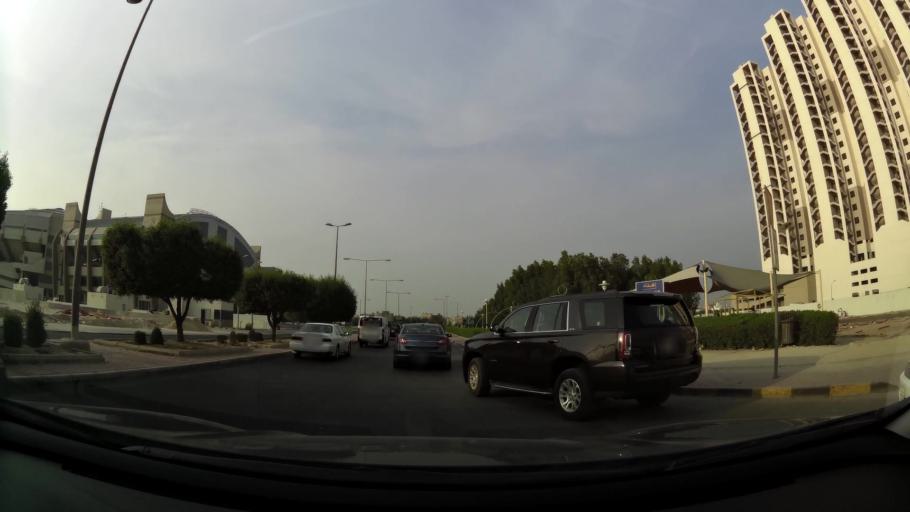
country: KW
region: Mubarak al Kabir
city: Sabah as Salim
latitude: 29.2646
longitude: 48.0767
